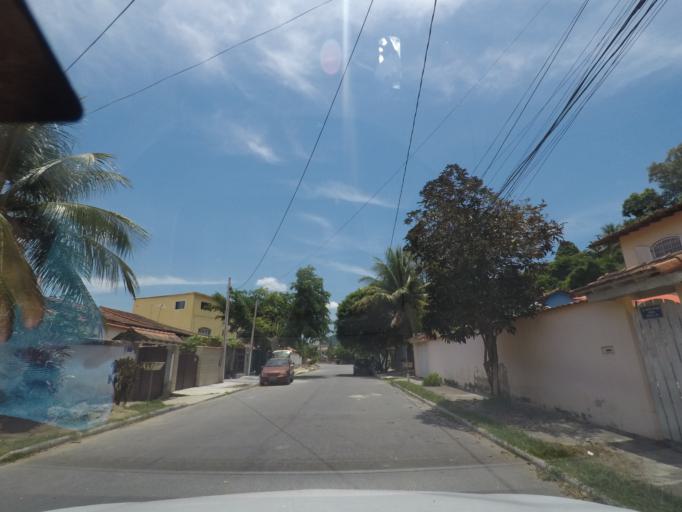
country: BR
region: Rio de Janeiro
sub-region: Marica
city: Marica
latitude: -22.9241
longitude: -42.8234
